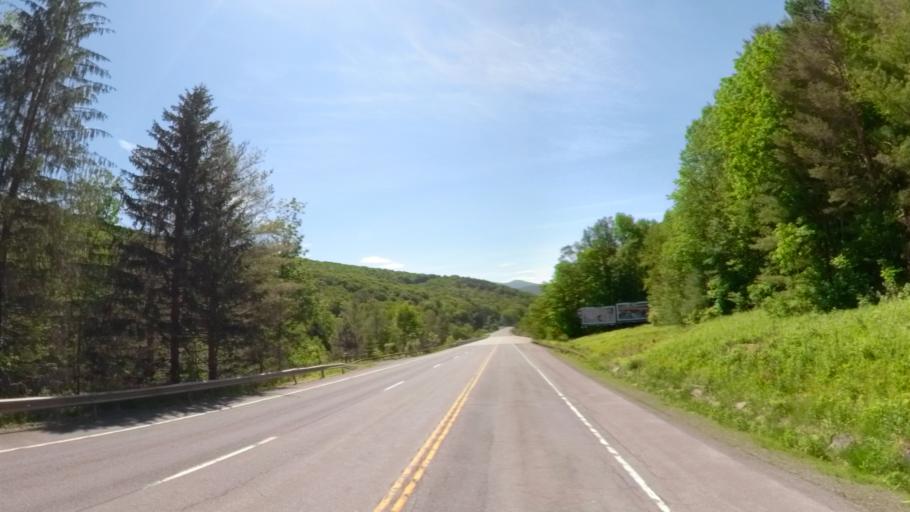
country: US
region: New York
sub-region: Delaware County
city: Stamford
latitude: 42.1368
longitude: -74.4804
